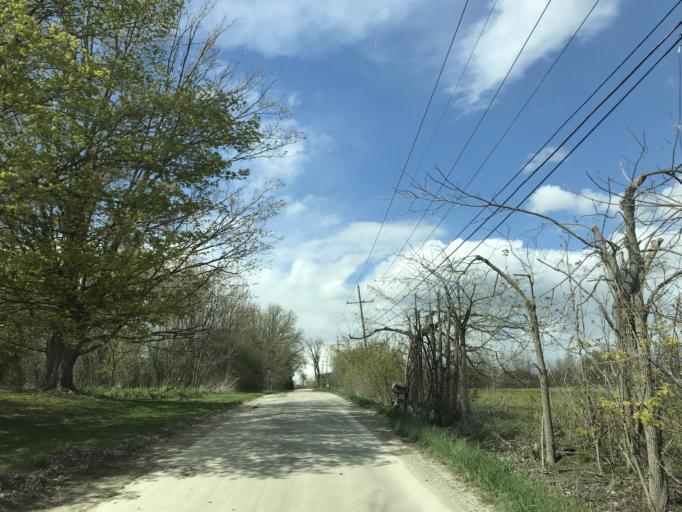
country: US
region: Michigan
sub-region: Oakland County
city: South Lyon
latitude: 42.3815
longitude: -83.6250
